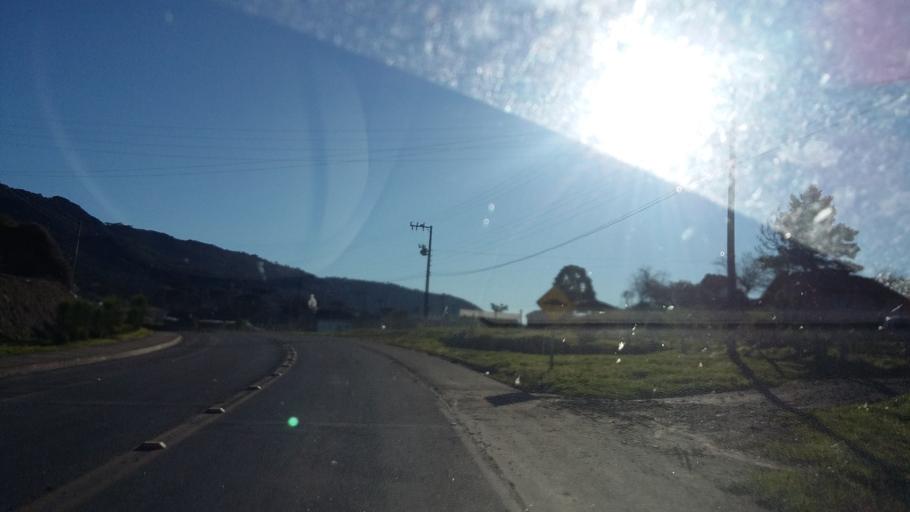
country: BR
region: Santa Catarina
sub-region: Lauro Muller
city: Lauro Muller
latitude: -28.0186
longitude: -49.5093
